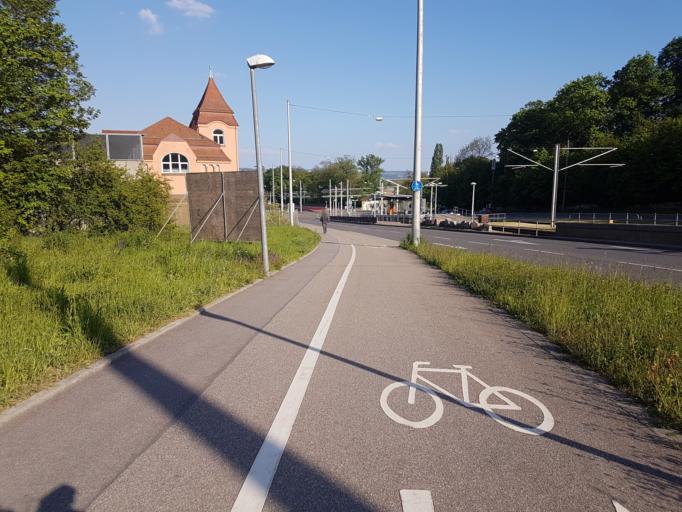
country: DE
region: Baden-Wuerttemberg
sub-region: Regierungsbezirk Stuttgart
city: Stuttgart
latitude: 48.8083
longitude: 9.1874
